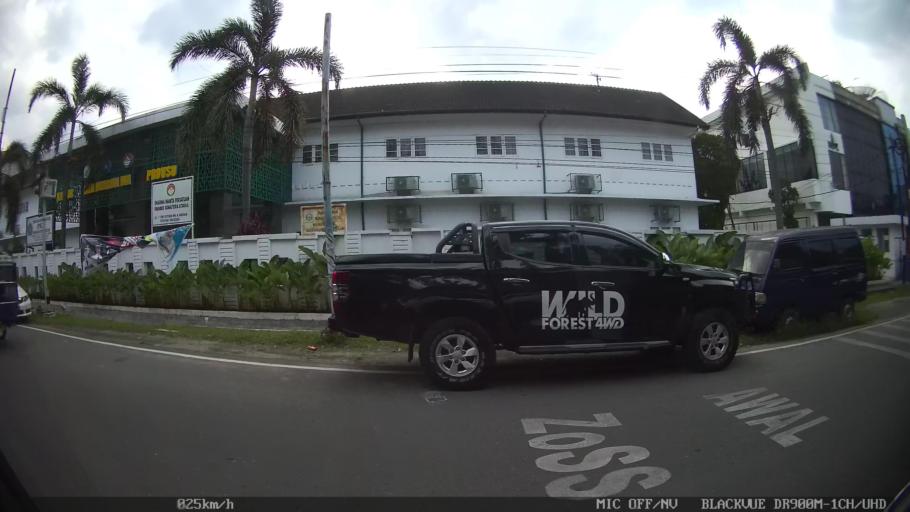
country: ID
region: North Sumatra
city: Medan
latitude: 3.5813
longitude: 98.6690
